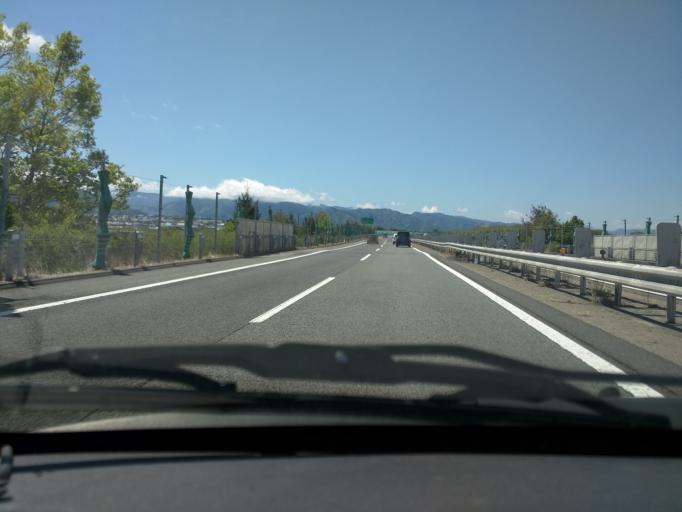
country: JP
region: Nagano
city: Nakano
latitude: 36.7201
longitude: 138.3137
